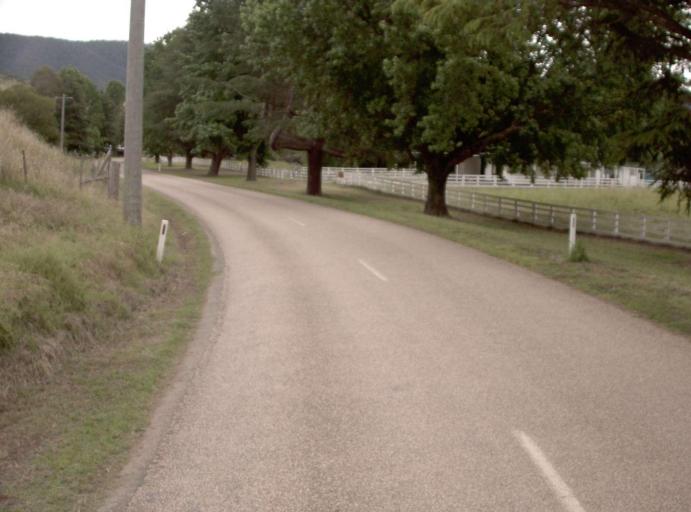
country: AU
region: Victoria
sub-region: East Gippsland
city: Bairnsdale
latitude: -37.4675
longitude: 147.2538
